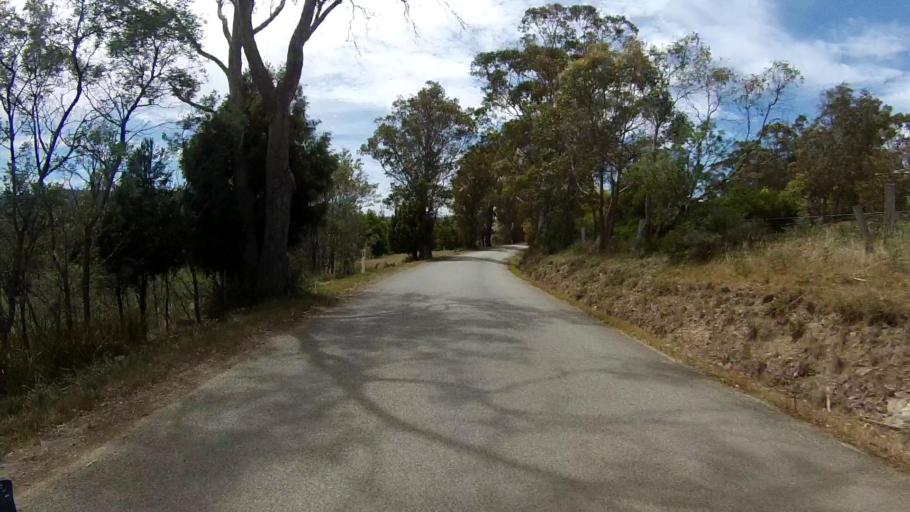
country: AU
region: Tasmania
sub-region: Sorell
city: Sorell
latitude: -42.7938
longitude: 147.6894
